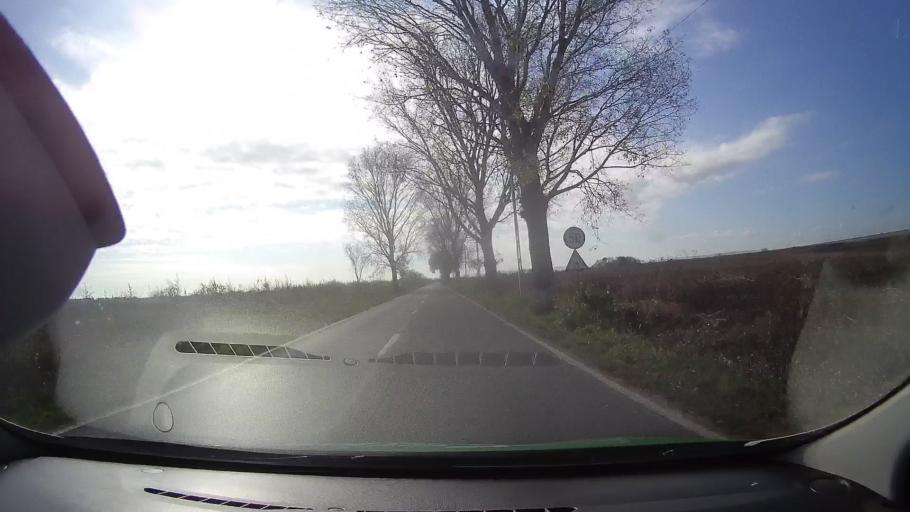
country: RO
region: Tulcea
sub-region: Comuna Valea Nucarilor
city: Agighiol
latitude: 44.9875
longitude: 28.8847
